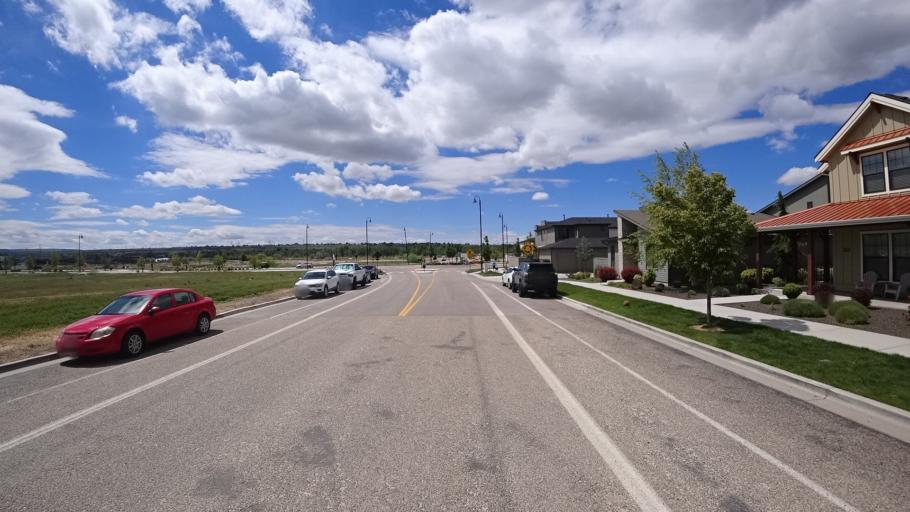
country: US
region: Idaho
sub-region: Ada County
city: Boise
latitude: 43.5750
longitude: -116.1332
